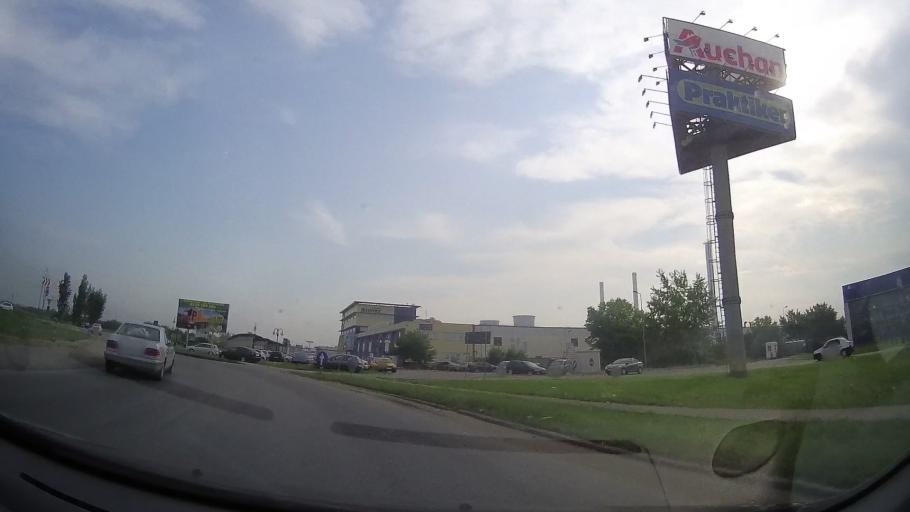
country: RO
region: Timis
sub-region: Comuna Giroc
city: Chisoda
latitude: 45.7056
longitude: 21.1868
